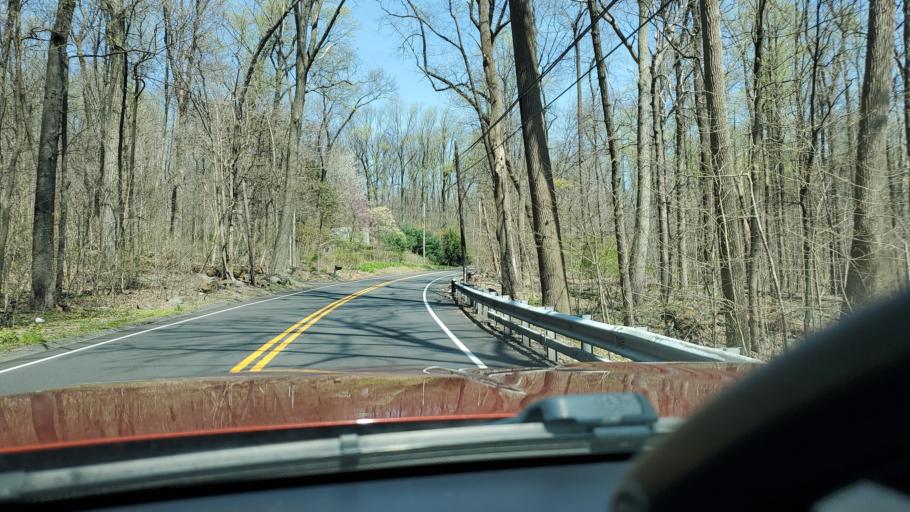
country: US
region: Pennsylvania
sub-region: Montgomery County
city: Pennsburg
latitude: 40.3516
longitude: -75.5405
